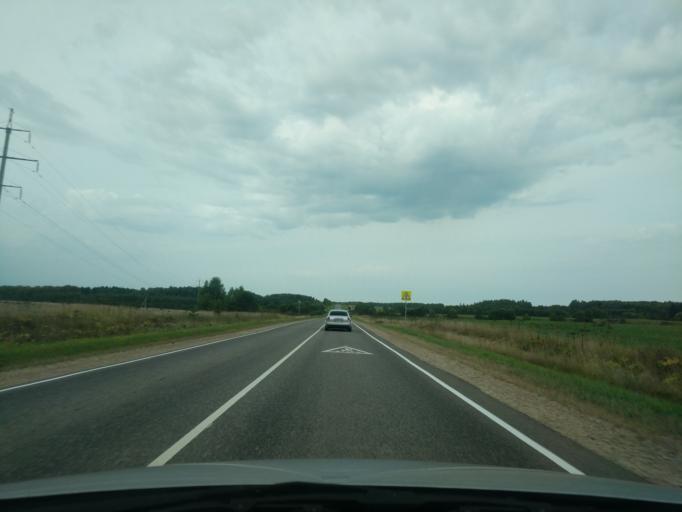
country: RU
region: Kirov
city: Mirnyy
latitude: 58.2725
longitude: 47.7902
